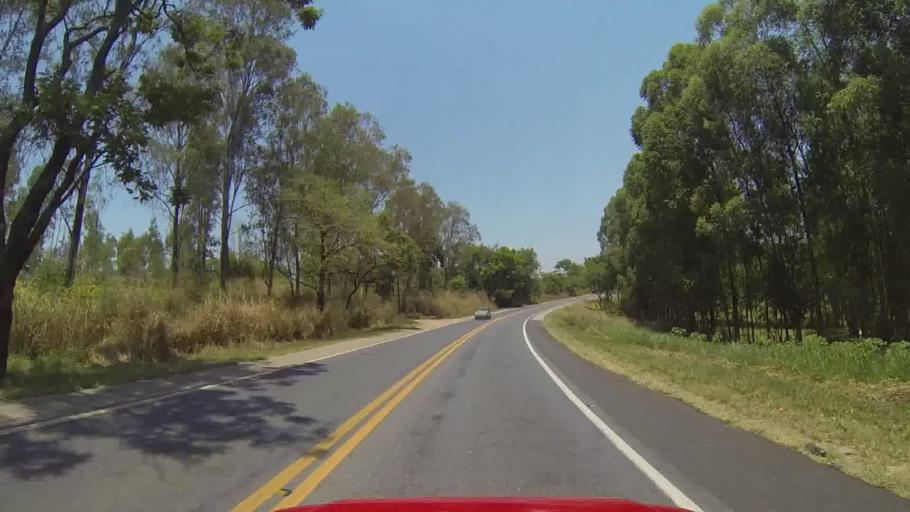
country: BR
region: Minas Gerais
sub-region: Itapecerica
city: Itapecerica
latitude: -20.3067
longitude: -45.2042
